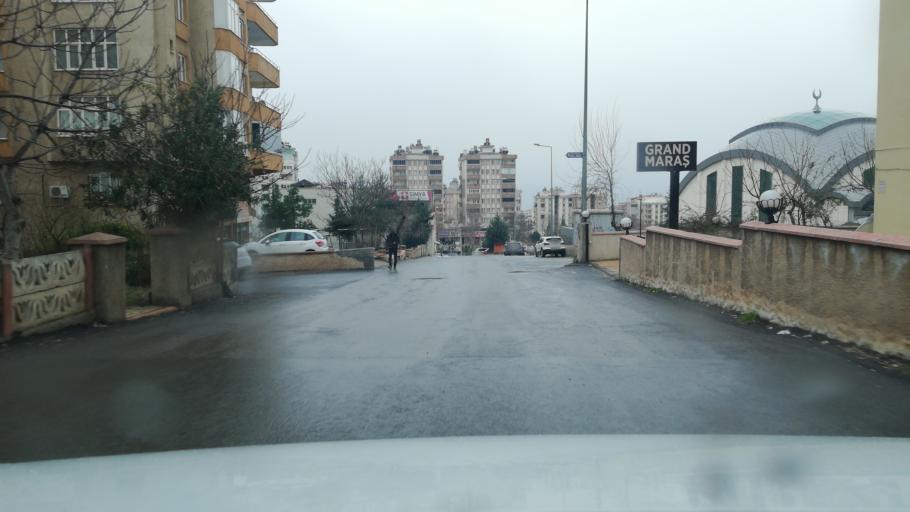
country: TR
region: Kahramanmaras
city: Kahramanmaras
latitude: 37.5903
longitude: 36.8831
